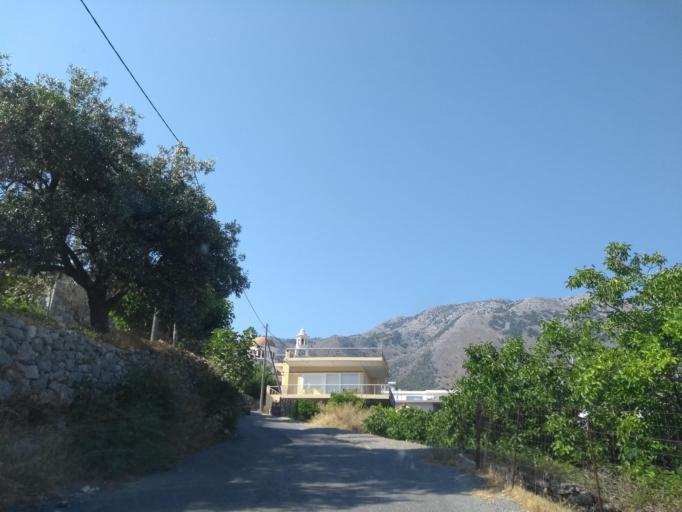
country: GR
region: Crete
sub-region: Nomos Chanias
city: Georgioupolis
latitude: 35.3162
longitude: 24.2957
